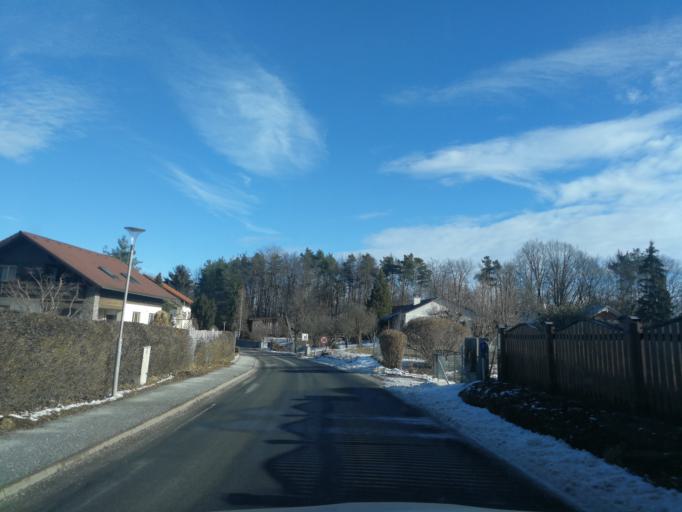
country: AT
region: Styria
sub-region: Politischer Bezirk Graz-Umgebung
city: Eggersdorf bei Graz
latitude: 47.0856
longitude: 15.5867
